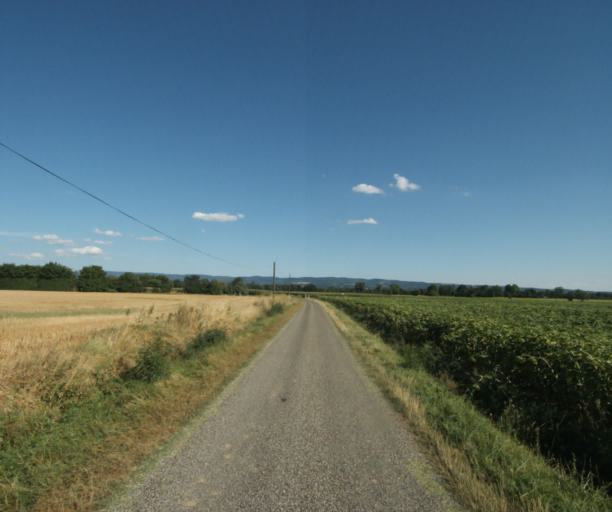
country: FR
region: Midi-Pyrenees
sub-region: Departement de la Haute-Garonne
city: Revel
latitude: 43.4874
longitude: 1.9477
